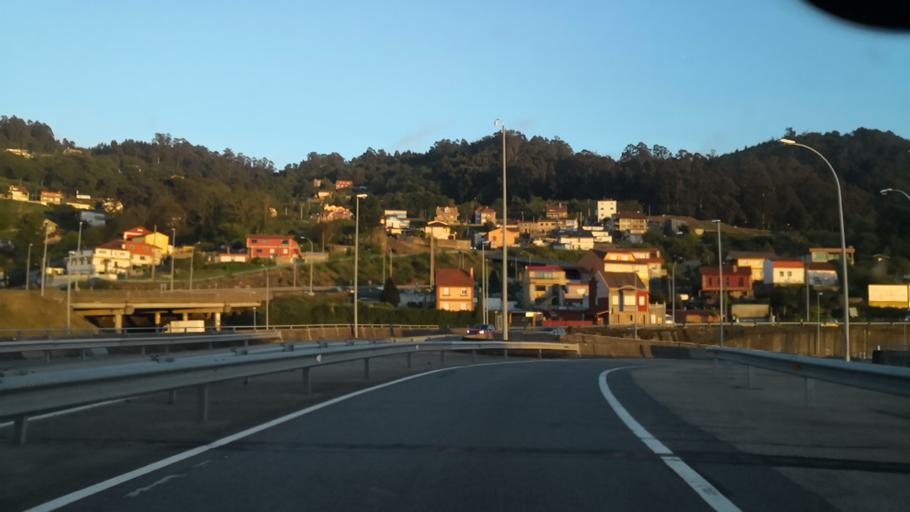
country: ES
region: Galicia
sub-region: Provincia de Pontevedra
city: Vigo
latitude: 42.2584
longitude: -8.6766
